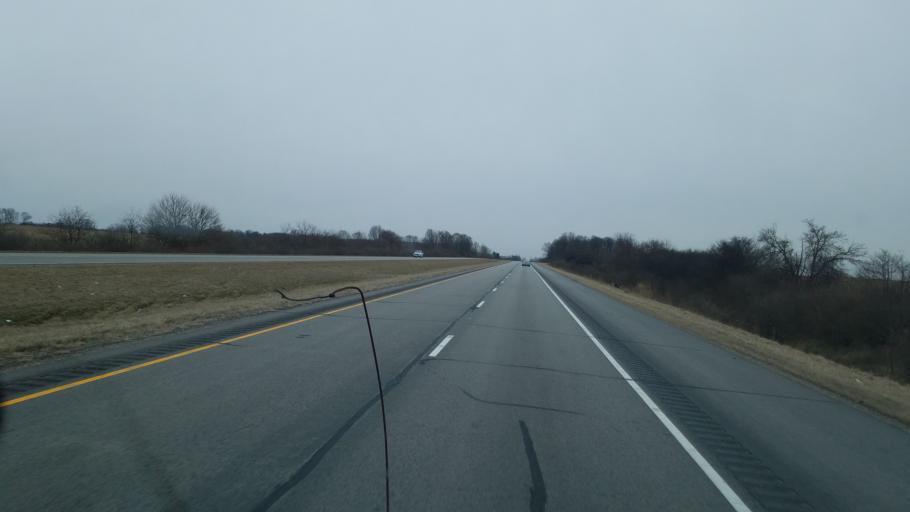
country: US
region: Indiana
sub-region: Marshall County
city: Argos
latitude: 41.1840
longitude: -86.2481
